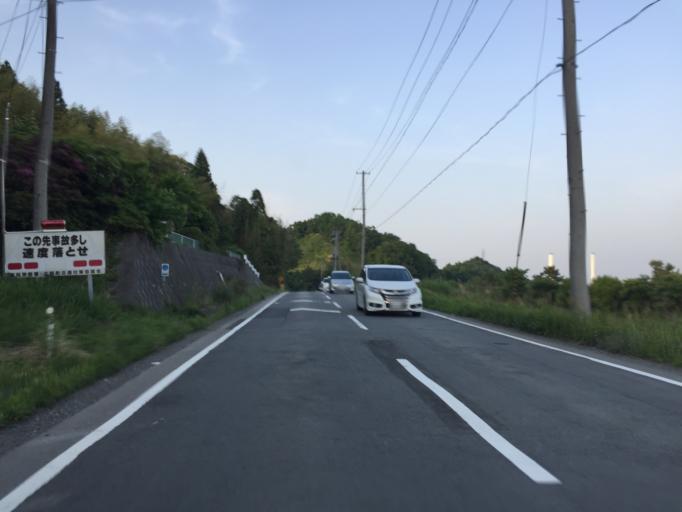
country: JP
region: Fukushima
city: Iwaki
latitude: 37.2275
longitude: 140.9760
